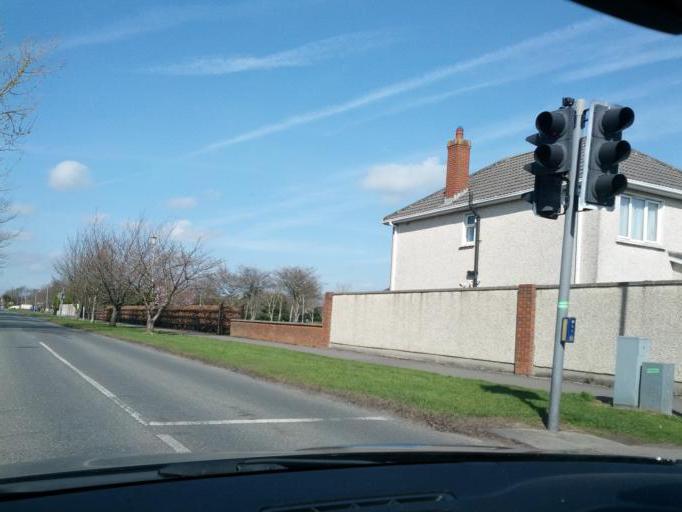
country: IE
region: Leinster
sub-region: Kildare
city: Maynooth
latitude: 53.3721
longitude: -6.5840
